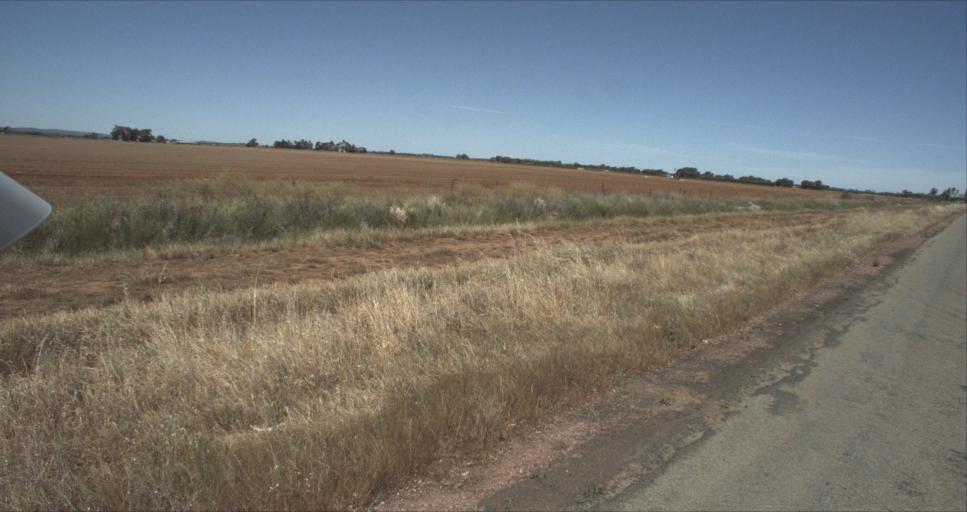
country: AU
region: New South Wales
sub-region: Leeton
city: Leeton
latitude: -34.5171
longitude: 146.3453
